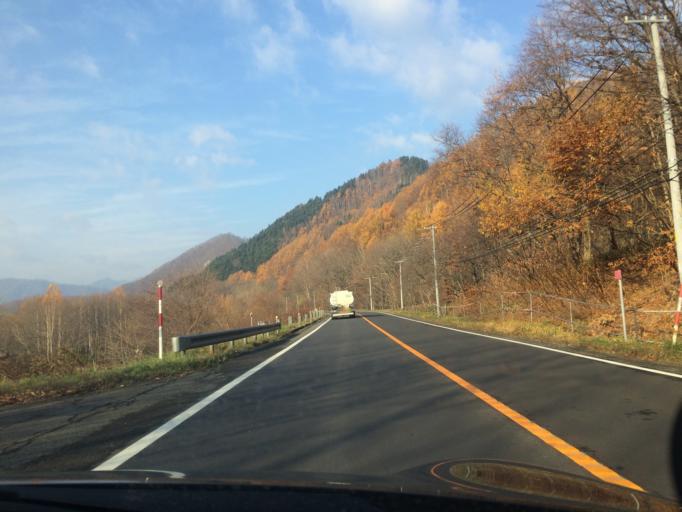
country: JP
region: Hokkaido
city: Shimo-furano
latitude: 42.8953
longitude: 142.4863
